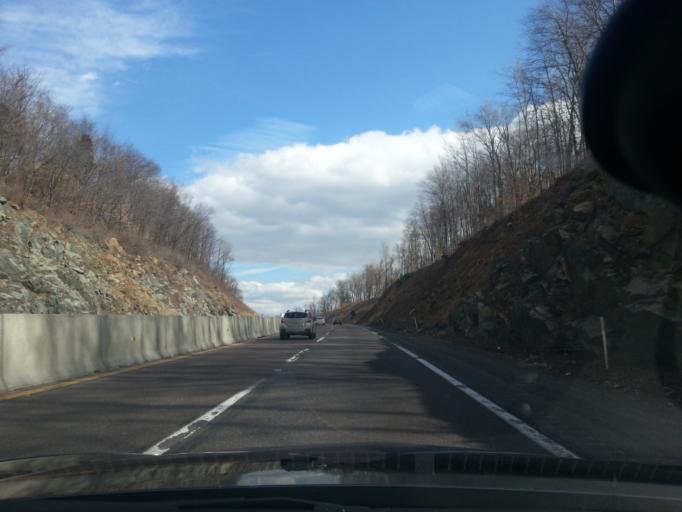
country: US
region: Pennsylvania
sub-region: Lehigh County
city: Emmaus
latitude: 40.4978
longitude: -75.4937
